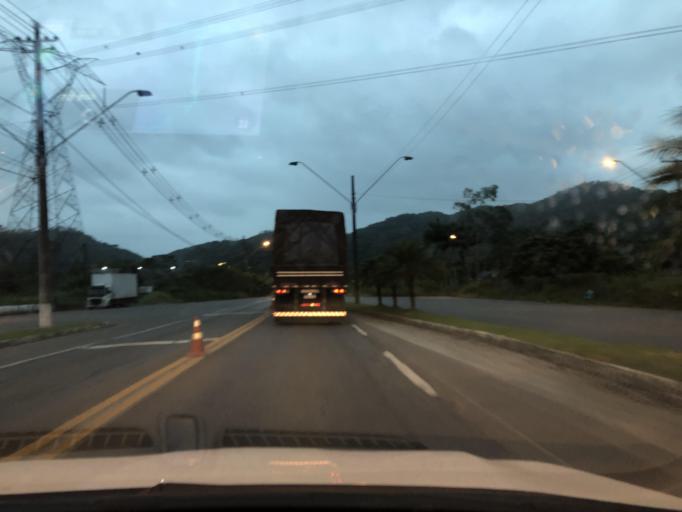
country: BR
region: Santa Catarina
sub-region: Pomerode
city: Pomerode
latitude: -26.7630
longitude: -49.0773
